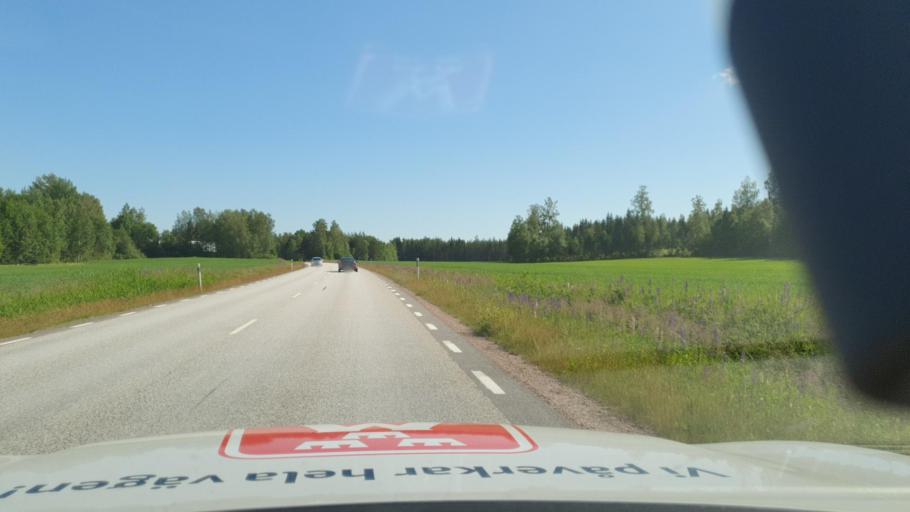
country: SE
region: Vaermland
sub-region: Storfors Kommun
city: Storfors
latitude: 59.5156
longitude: 14.3029
